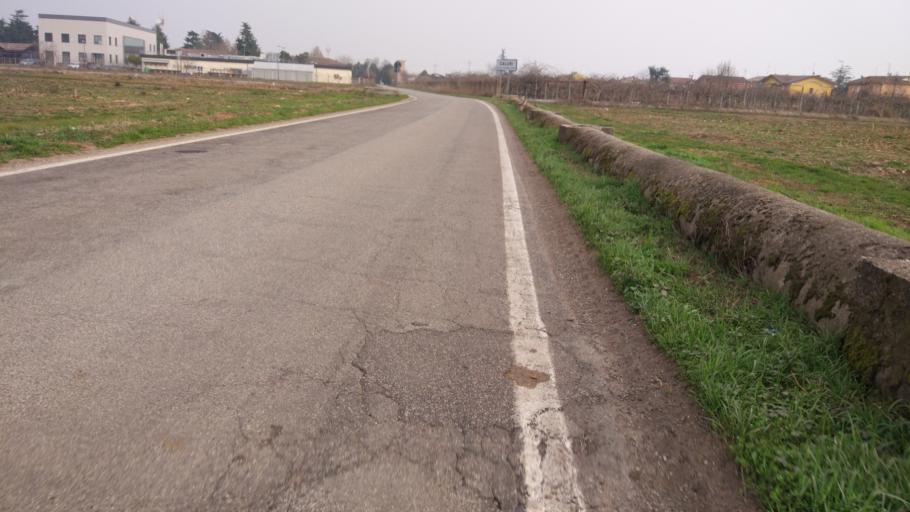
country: IT
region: Veneto
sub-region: Provincia di Verona
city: Villafranca di Verona
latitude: 45.3822
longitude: 10.8735
